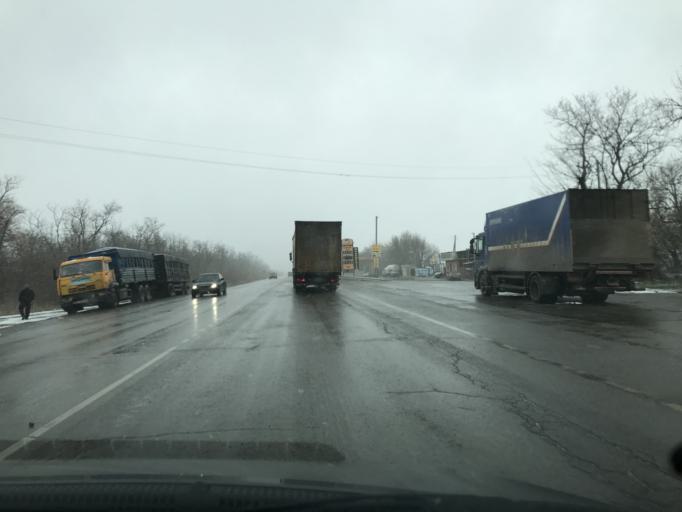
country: RU
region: Rostov
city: Bataysk
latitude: 47.0653
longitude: 39.8068
